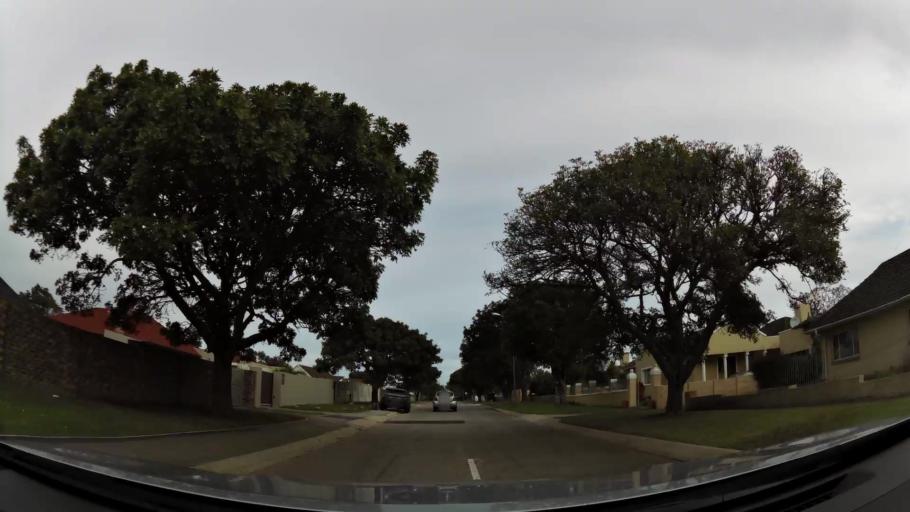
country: ZA
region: Eastern Cape
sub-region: Nelson Mandela Bay Metropolitan Municipality
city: Port Elizabeth
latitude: -33.9430
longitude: 25.5009
